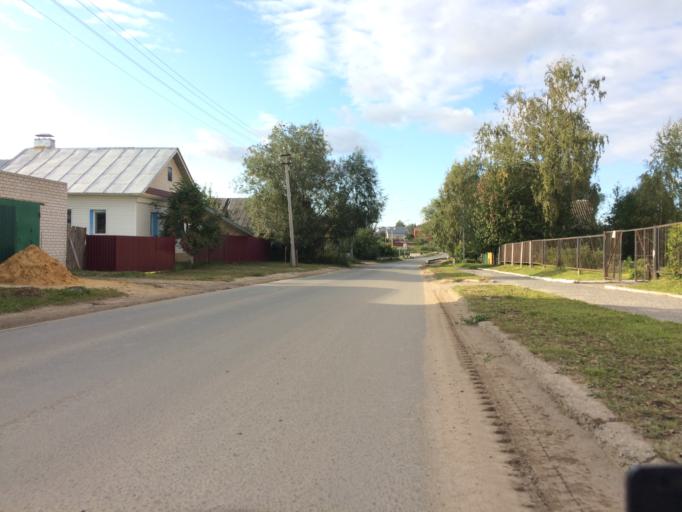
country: RU
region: Mariy-El
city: Yoshkar-Ola
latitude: 56.6469
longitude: 47.9815
